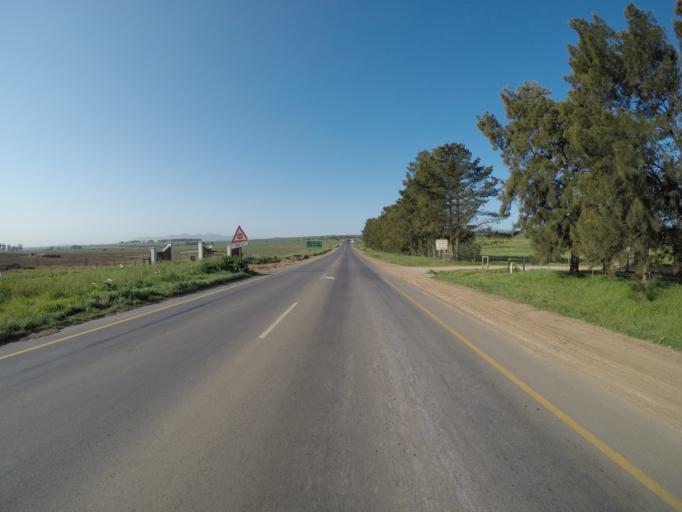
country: ZA
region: Western Cape
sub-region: City of Cape Town
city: Kraaifontein
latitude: -33.7715
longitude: 18.7537
